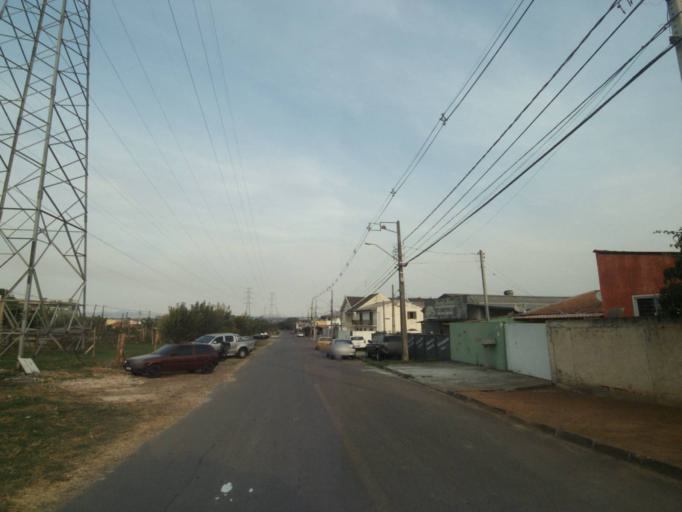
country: BR
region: Parana
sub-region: Pinhais
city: Pinhais
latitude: -25.4834
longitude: -49.2036
